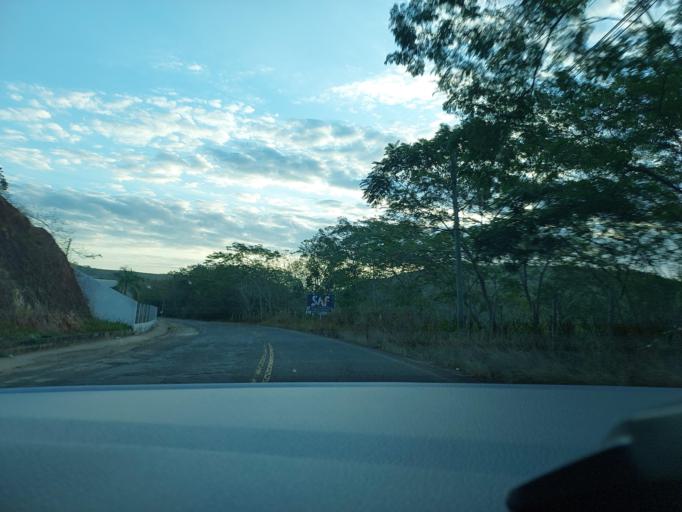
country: BR
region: Rio de Janeiro
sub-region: Natividade
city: Natividade
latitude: -21.1997
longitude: -42.1212
